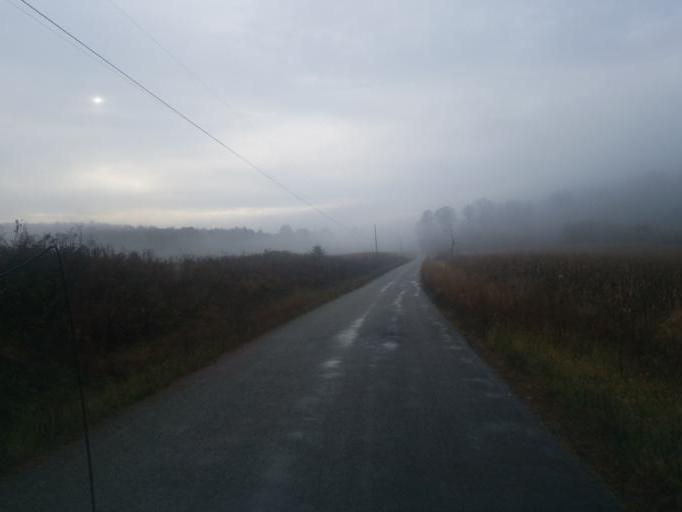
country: US
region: Ohio
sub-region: Athens County
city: Glouster
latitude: 39.4677
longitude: -81.9381
